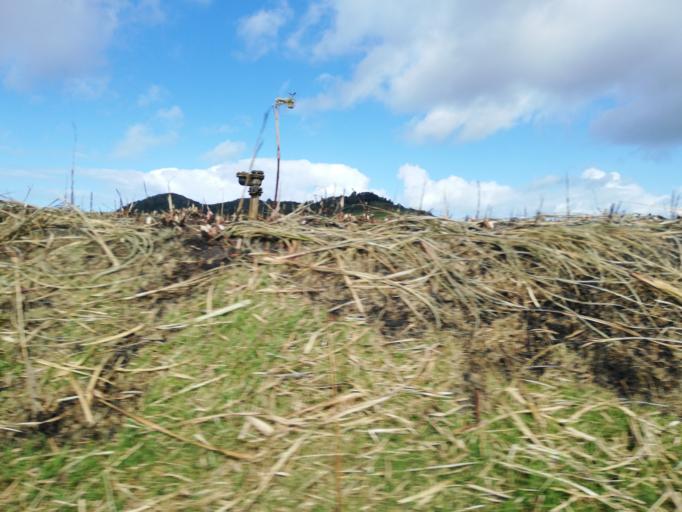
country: MU
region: Flacq
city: Grande Riviere Sud Est
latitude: -20.2838
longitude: 57.7552
